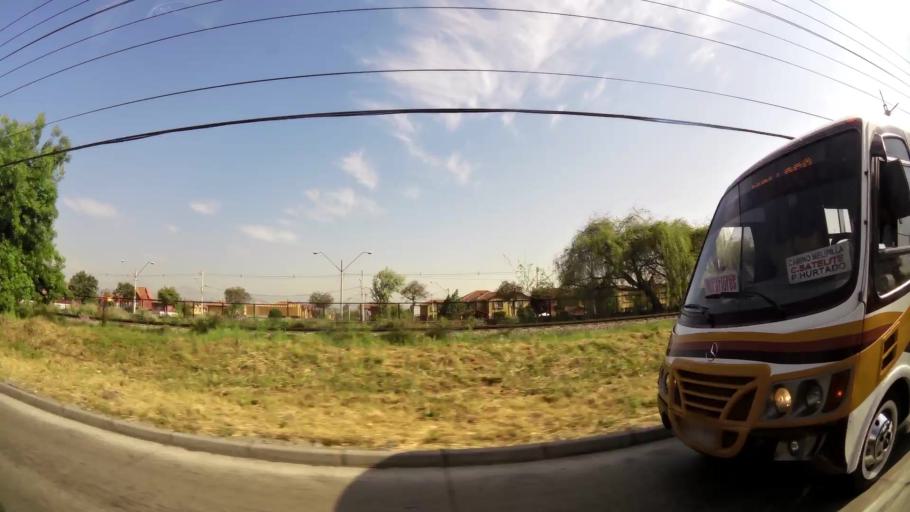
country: CL
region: Santiago Metropolitan
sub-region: Provincia de Maipo
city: San Bernardo
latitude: -33.5466
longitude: -70.7851
